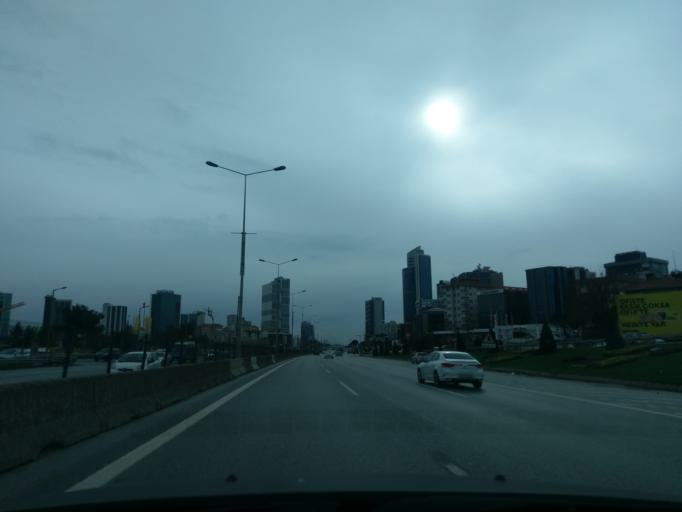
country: TR
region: Istanbul
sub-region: Atasehir
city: Atasehir
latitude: 40.9792
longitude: 29.0966
